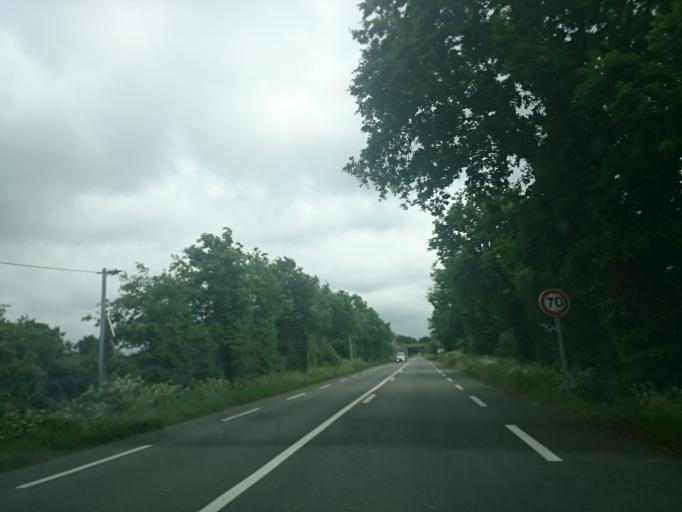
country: FR
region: Pays de la Loire
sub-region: Departement de la Loire-Atlantique
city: La Montagne
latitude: 47.1722
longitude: -1.6788
